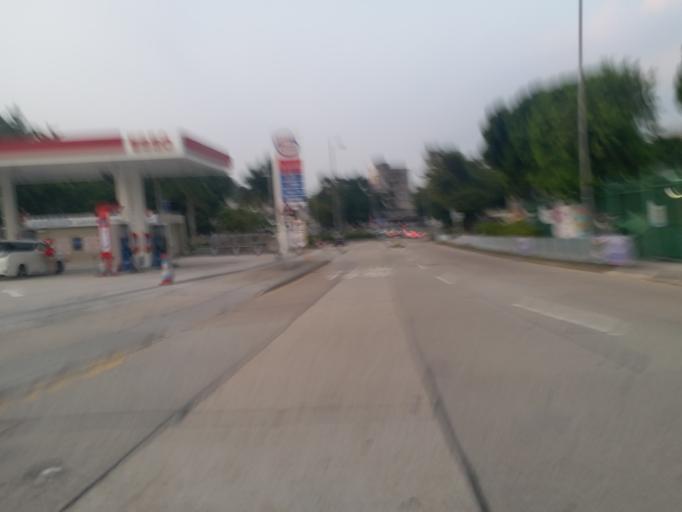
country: HK
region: Yuen Long
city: Yuen Long Kau Hui
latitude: 22.4411
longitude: 114.0111
